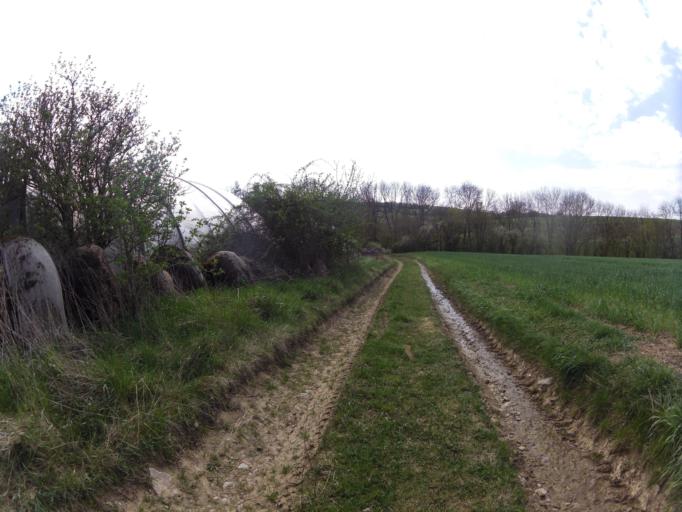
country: DE
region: Bavaria
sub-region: Regierungsbezirk Unterfranken
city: Winterhausen
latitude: 49.6770
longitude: 10.0052
